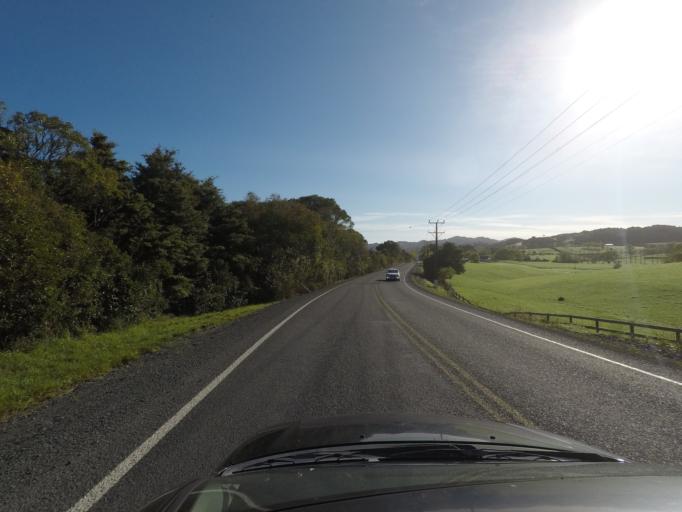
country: NZ
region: Auckland
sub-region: Auckland
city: Red Hill
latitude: -36.9925
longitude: 174.9854
